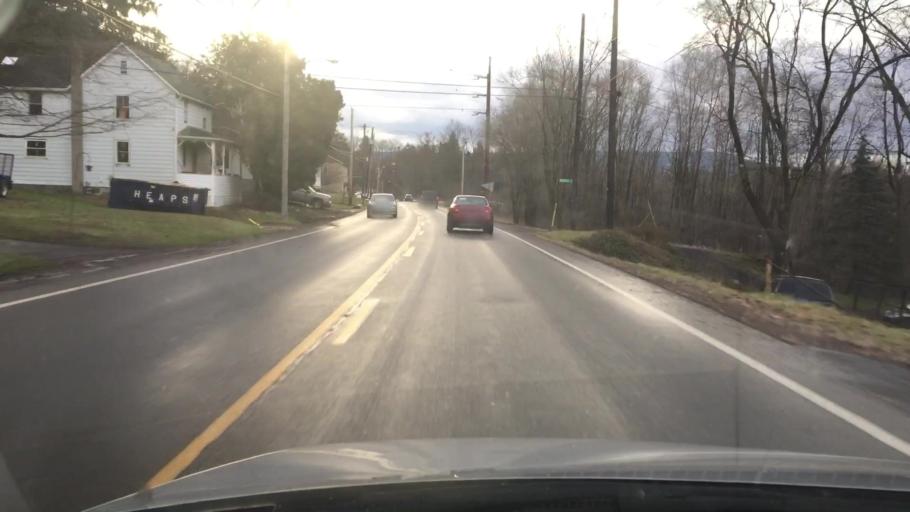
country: US
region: Pennsylvania
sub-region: Columbia County
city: Bloomsburg
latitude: 41.0104
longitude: -76.4649
